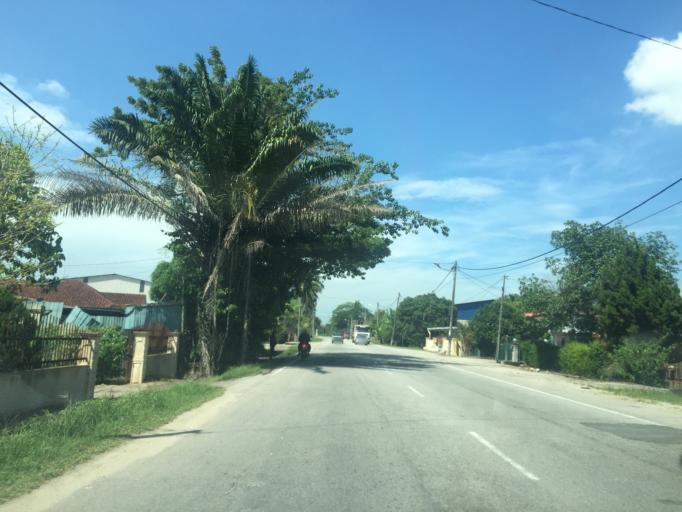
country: MY
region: Penang
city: Tasek Glugor
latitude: 5.4885
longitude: 100.4705
